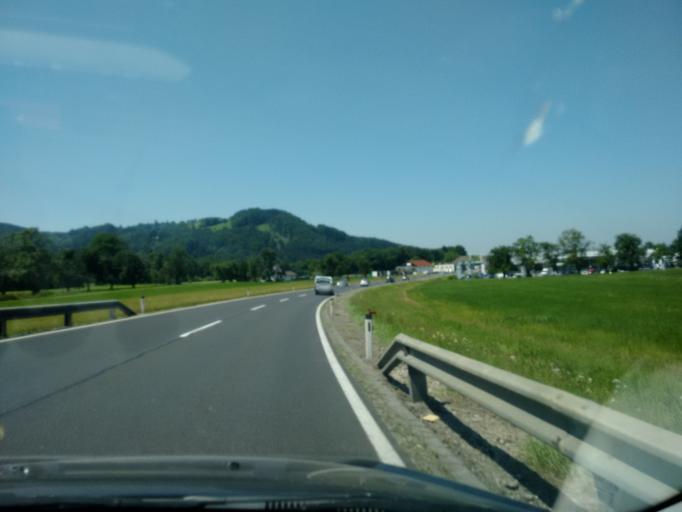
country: AT
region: Upper Austria
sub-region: Politischer Bezirk Gmunden
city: Altmunster
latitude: 47.9356
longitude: 13.7600
